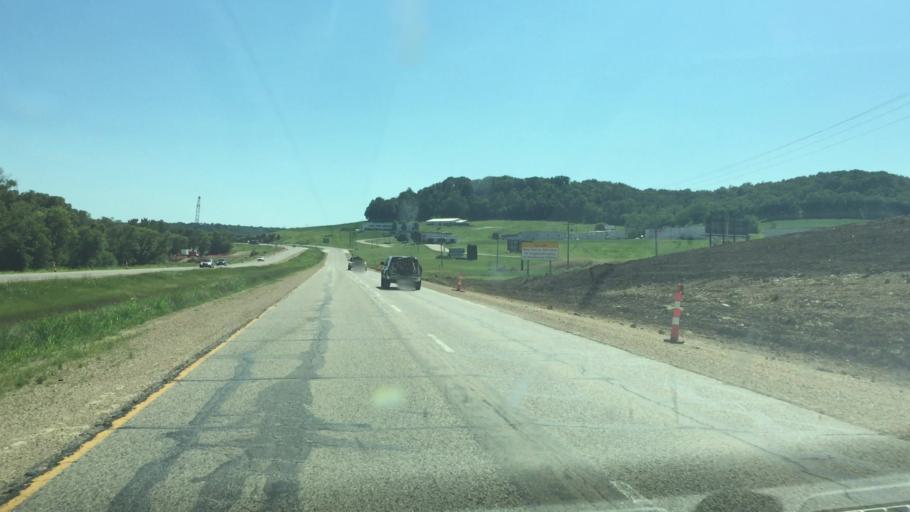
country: US
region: Iowa
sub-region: Dubuque County
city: Dubuque
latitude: 42.4321
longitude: -90.6858
